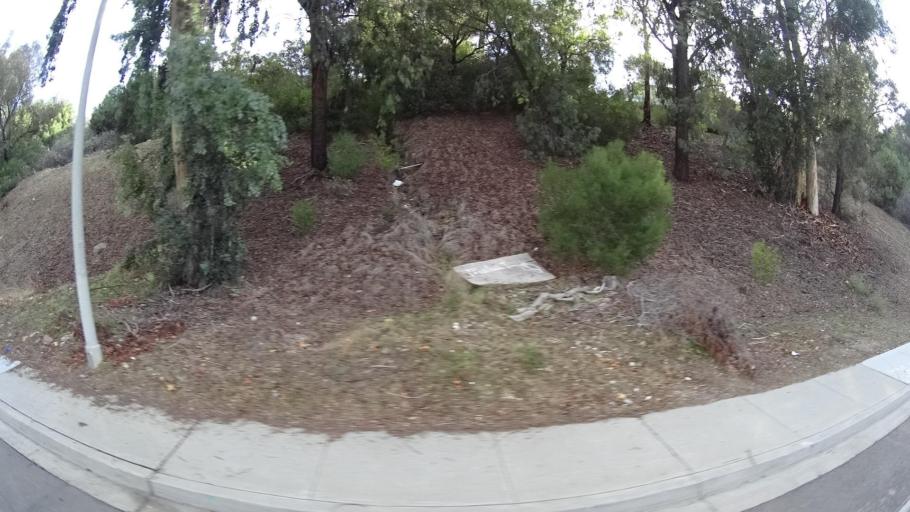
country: US
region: California
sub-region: San Diego County
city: Spring Valley
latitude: 32.7281
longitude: -116.9708
